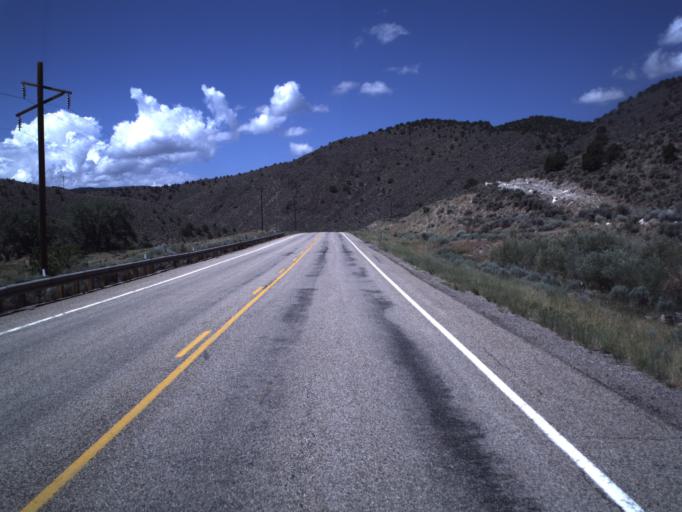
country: US
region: Utah
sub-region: Piute County
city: Junction
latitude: 38.1418
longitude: -112.3079
